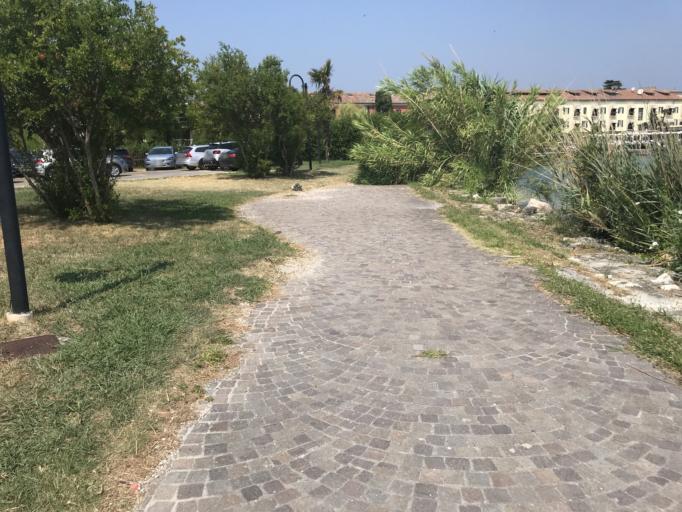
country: IT
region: Lombardy
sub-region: Provincia di Brescia
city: Sirmione
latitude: 45.4898
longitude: 10.6102
